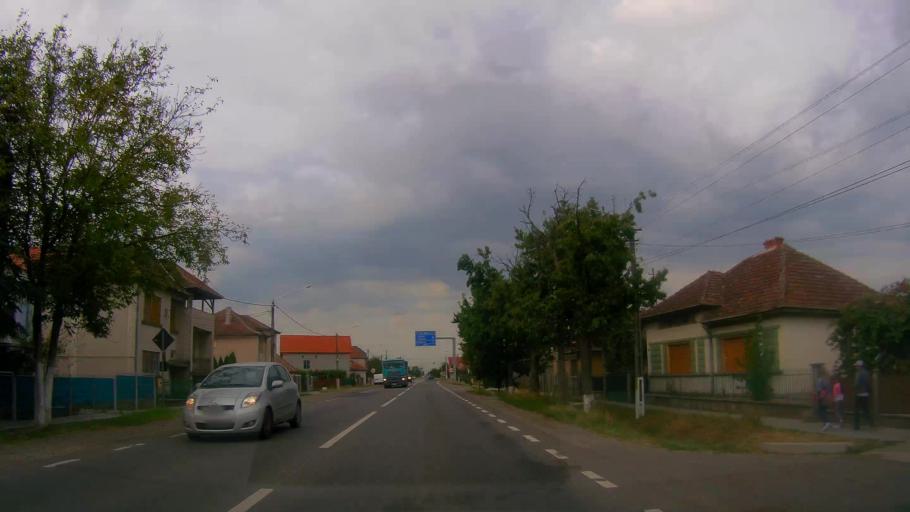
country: RO
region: Satu Mare
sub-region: Comuna Botiz
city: Botiz
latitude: 47.8277
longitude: 22.9499
